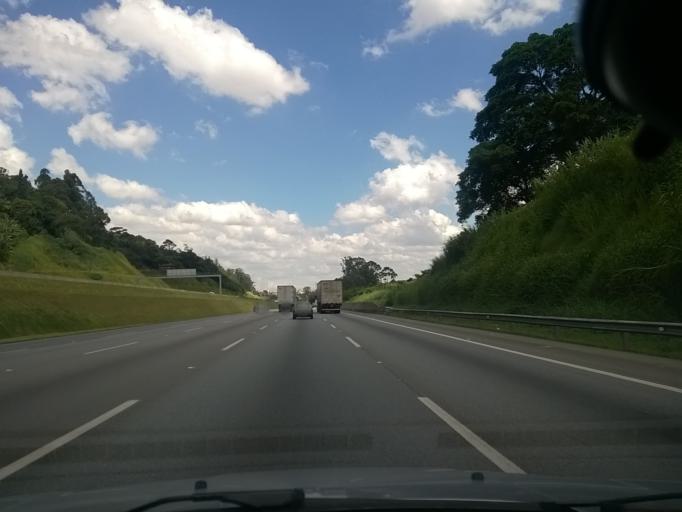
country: BR
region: Sao Paulo
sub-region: Osasco
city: Osasco
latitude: -23.4554
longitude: -46.7539
